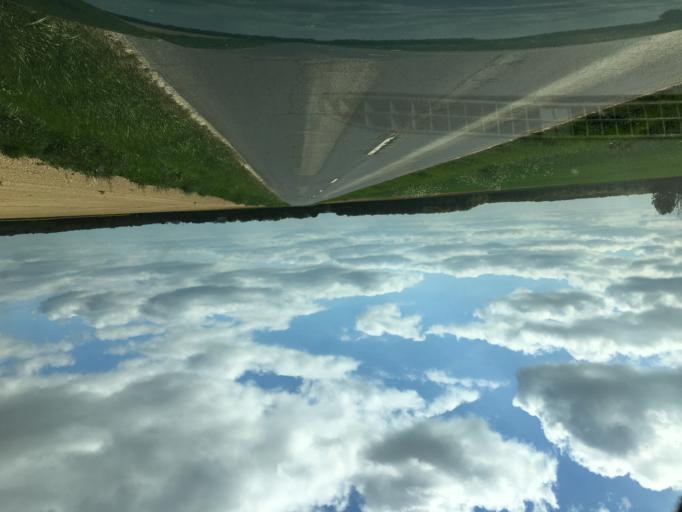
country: FR
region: Centre
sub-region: Departement du Loir-et-Cher
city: Saint-Ouen
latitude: 47.7840
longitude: 1.1274
